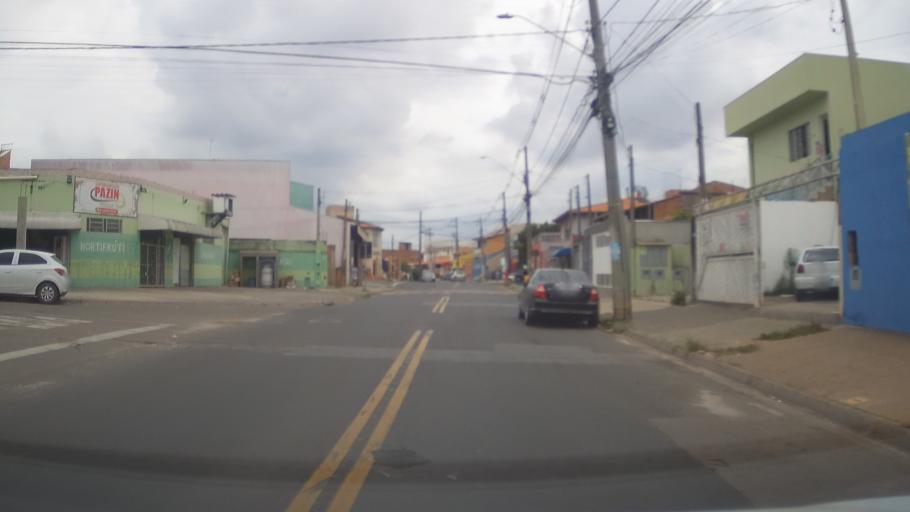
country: BR
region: Sao Paulo
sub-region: Itupeva
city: Itupeva
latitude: -23.1435
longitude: -47.0064
